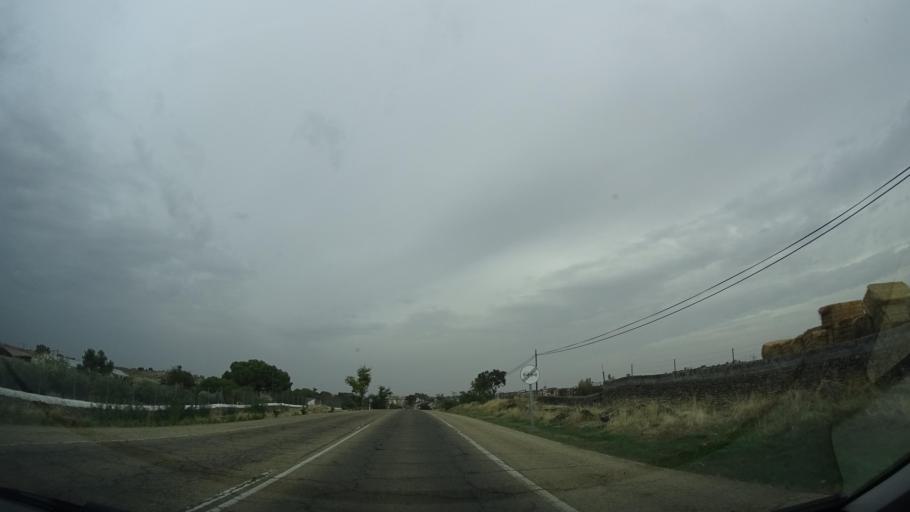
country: ES
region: Extremadura
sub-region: Provincia de Caceres
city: Trujillo
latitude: 39.4700
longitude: -5.8621
